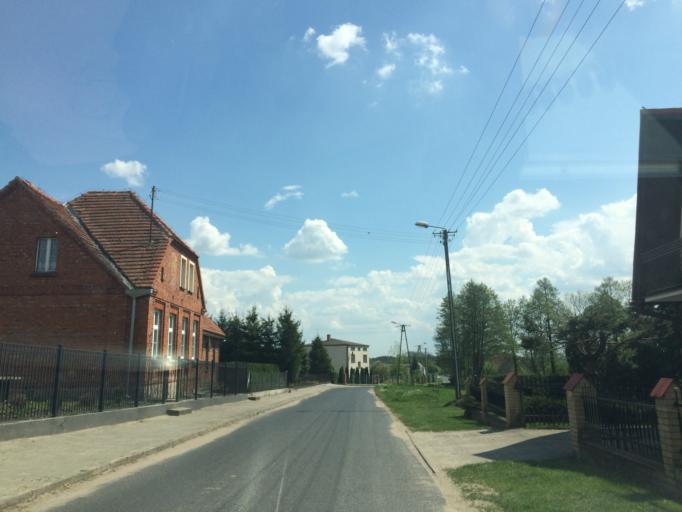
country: PL
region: Warmian-Masurian Voivodeship
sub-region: Powiat nowomiejski
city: Nowe Miasto Lubawskie
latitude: 53.4499
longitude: 19.5607
